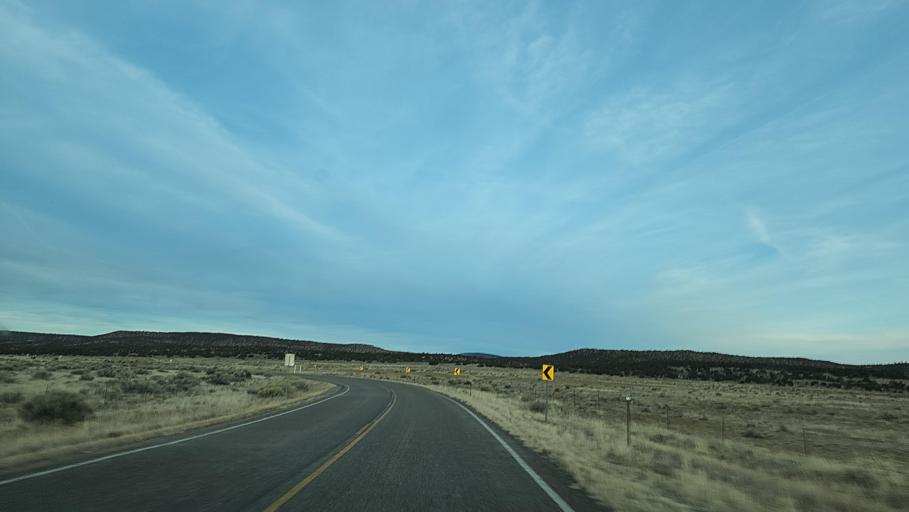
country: US
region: New Mexico
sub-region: Cibola County
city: Grants
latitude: 34.7103
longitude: -107.9911
